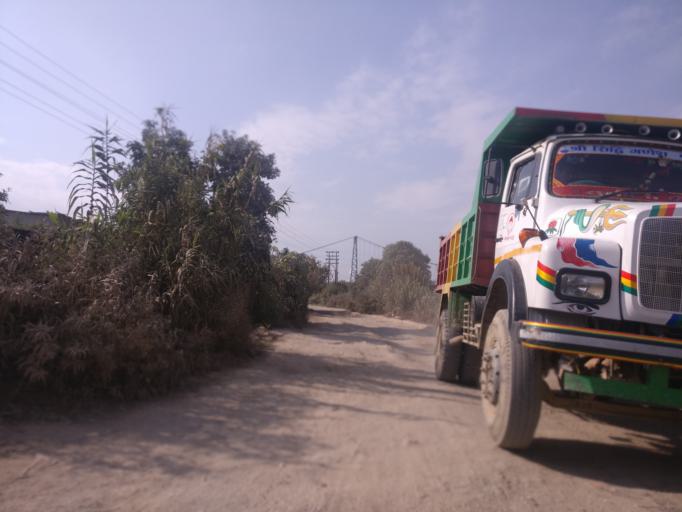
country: NP
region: Central Region
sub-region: Bagmati Zone
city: Patan
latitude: 27.6748
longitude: 85.3391
